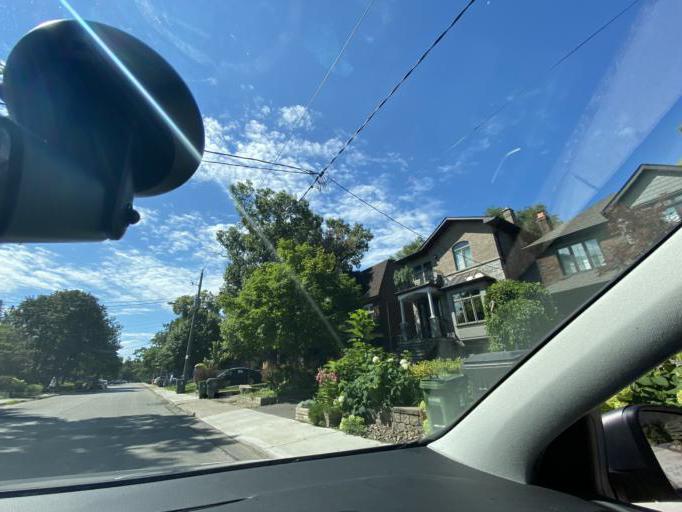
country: CA
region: Ontario
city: Etobicoke
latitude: 43.6621
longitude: -79.4937
